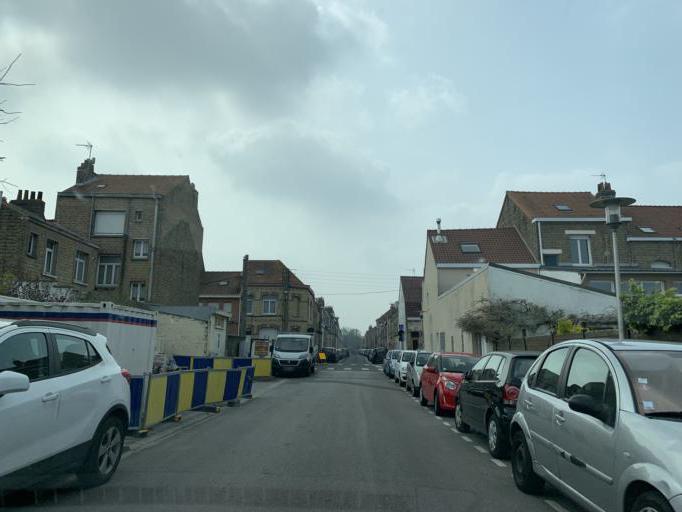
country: FR
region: Nord-Pas-de-Calais
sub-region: Departement du Nord
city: Coudekerque-Branche
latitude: 51.0371
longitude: 2.4041
